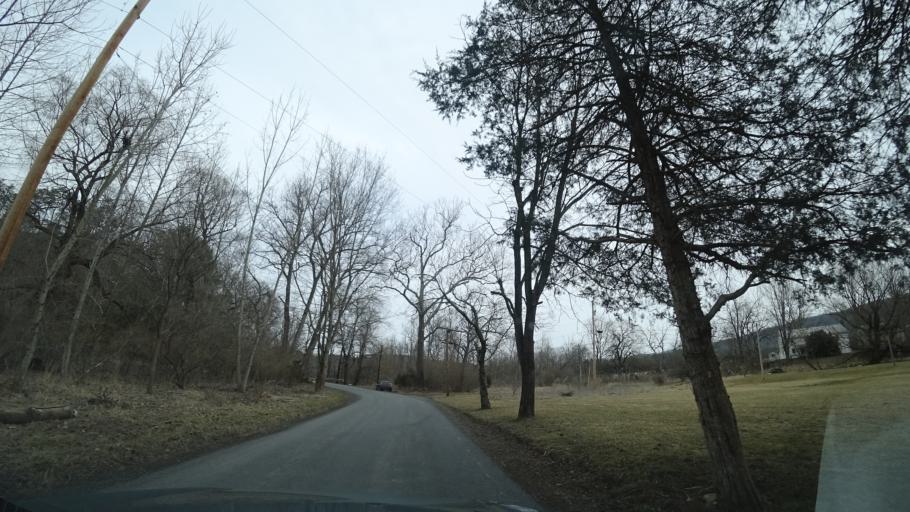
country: US
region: Virginia
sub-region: Shenandoah County
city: Woodstock
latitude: 39.0686
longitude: -78.6296
